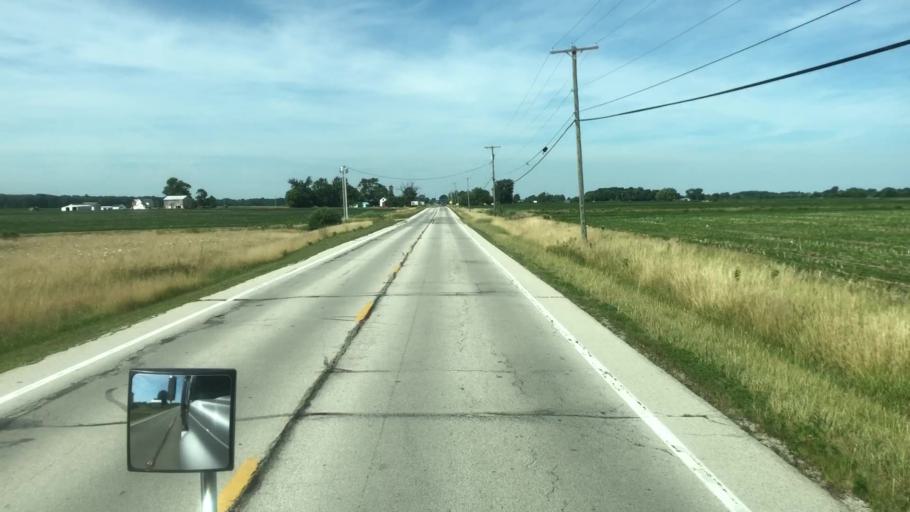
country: US
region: Ohio
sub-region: Ottawa County
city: Port Clinton
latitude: 41.4283
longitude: -82.8562
